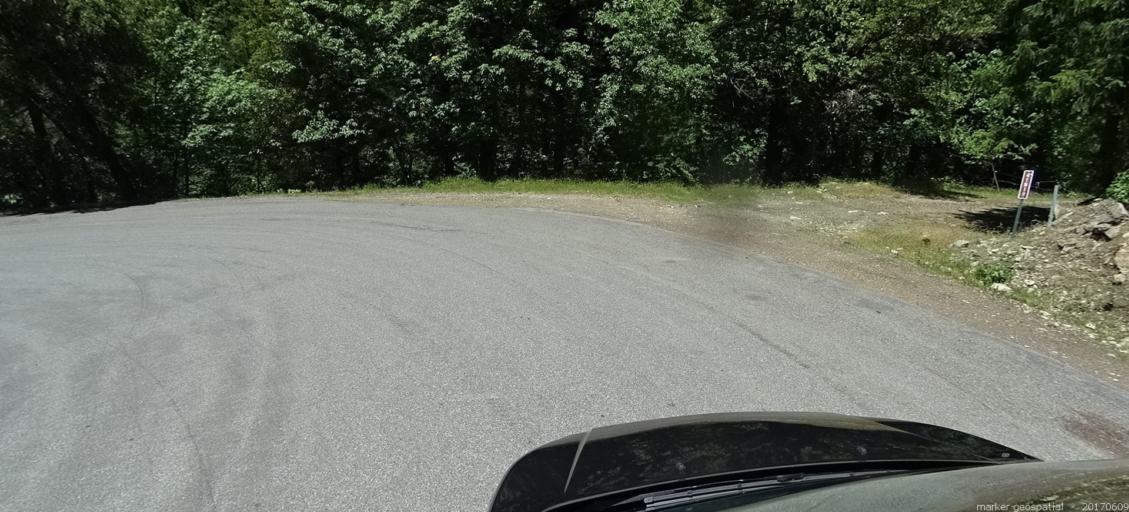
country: US
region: California
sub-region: Siskiyou County
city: Yreka
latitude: 41.3788
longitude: -123.0190
